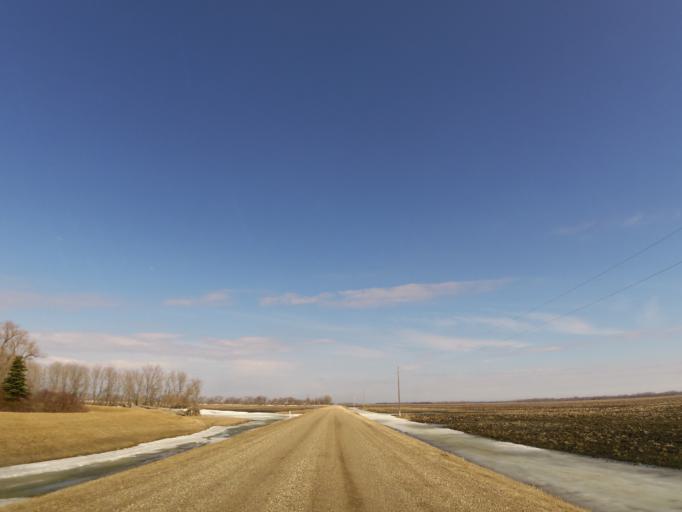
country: US
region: North Dakota
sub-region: Walsh County
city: Grafton
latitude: 48.3946
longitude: -97.1684
